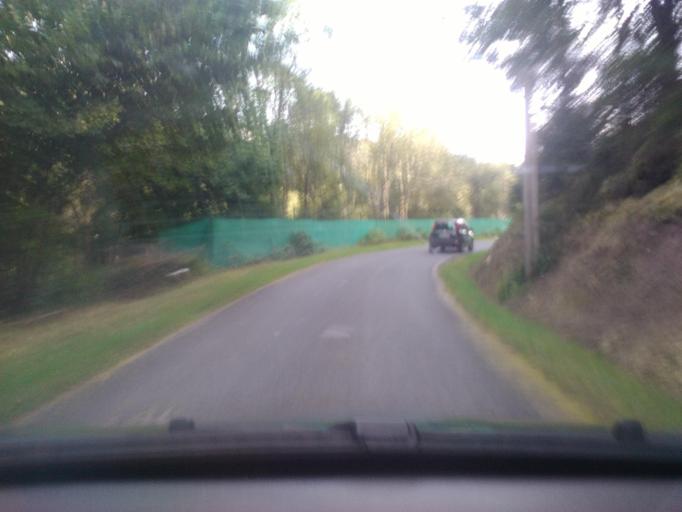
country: FR
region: Lorraine
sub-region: Departement des Vosges
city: Taintrux
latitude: 48.2517
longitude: 6.8329
